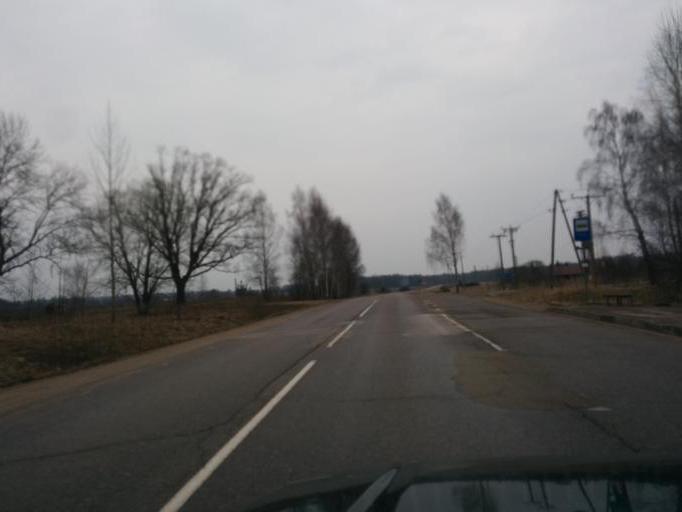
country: LV
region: Ikskile
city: Ikskile
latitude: 56.8205
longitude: 24.4473
